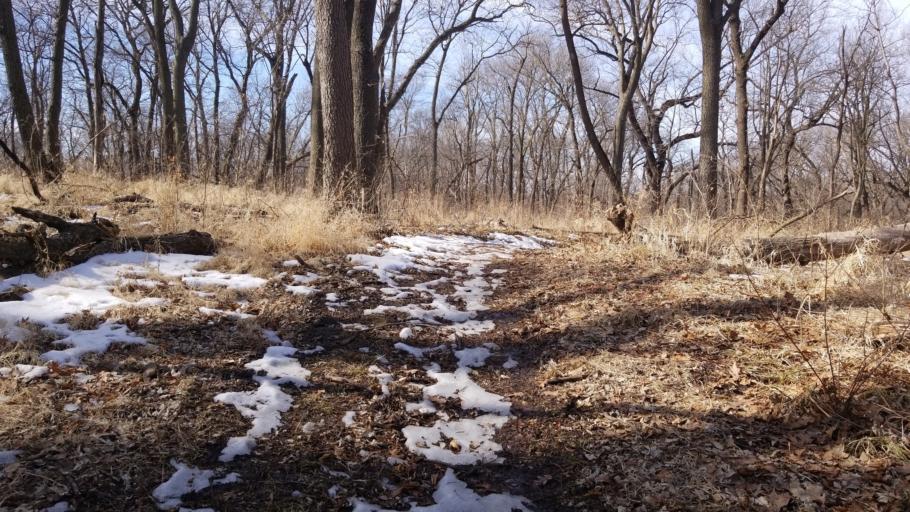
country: US
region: Nebraska
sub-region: Sarpy County
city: Bellevue
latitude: 41.1719
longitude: -95.9006
